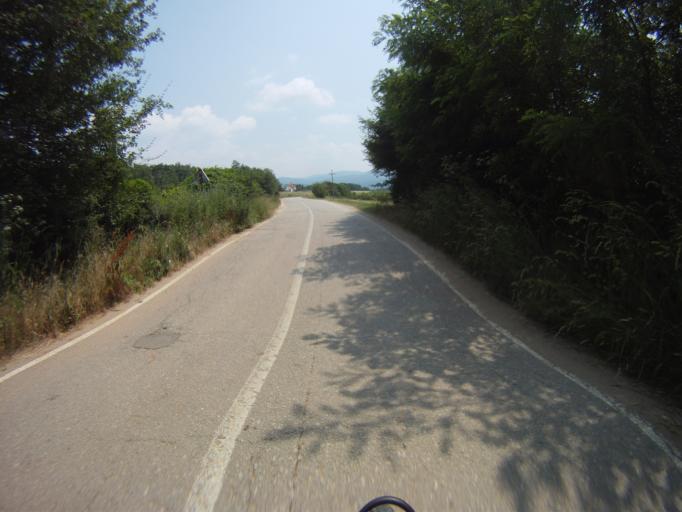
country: RS
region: Central Serbia
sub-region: Nisavski Okrug
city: Gadzin Han
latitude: 43.2041
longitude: 21.9657
